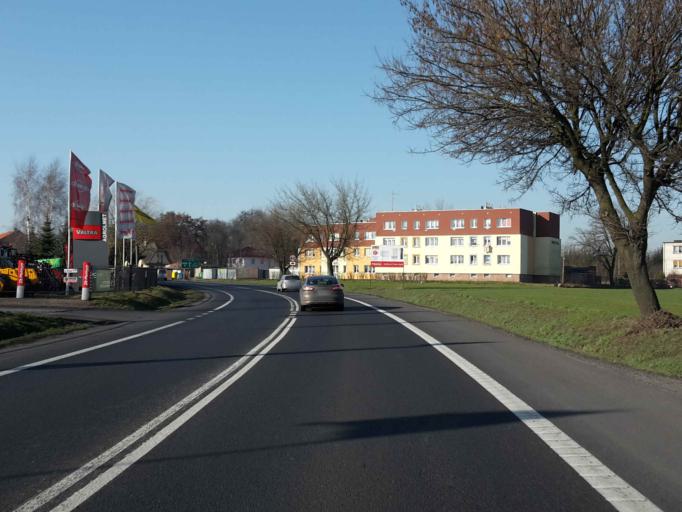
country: PL
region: Kujawsko-Pomorskie
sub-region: Powiat inowroclawski
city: Gniewkowo
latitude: 52.8971
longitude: 18.4054
